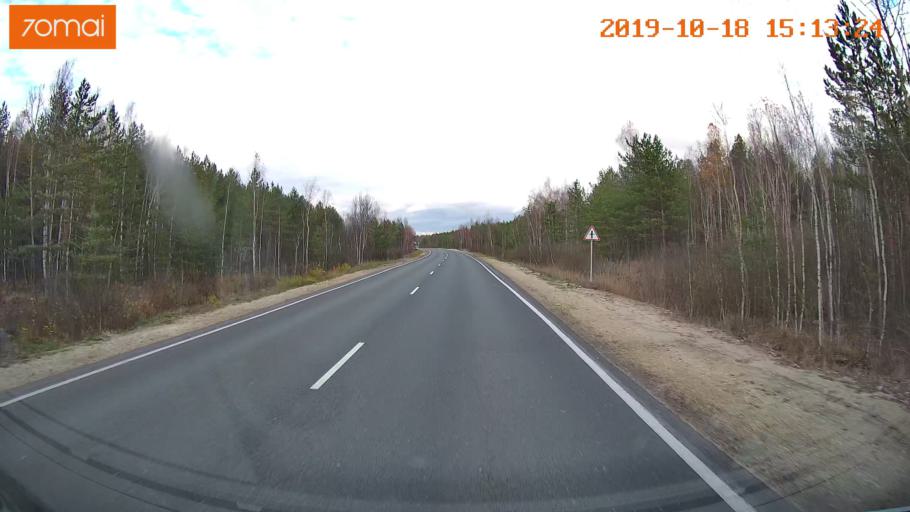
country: RU
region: Vladimir
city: Gus'-Khrustal'nyy
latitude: 55.5864
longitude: 40.7164
